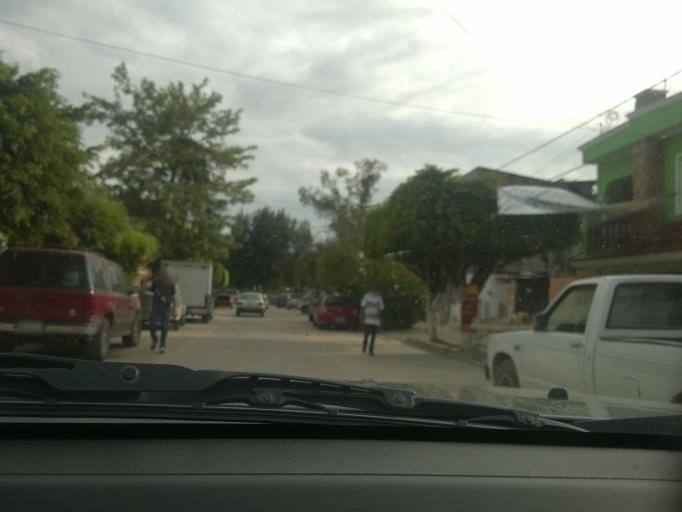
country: MX
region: Guanajuato
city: Leon
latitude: 21.1271
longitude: -101.6988
